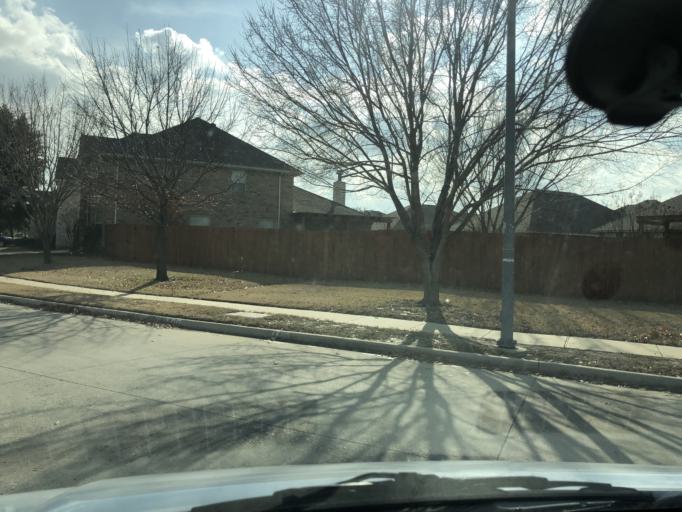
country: US
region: Texas
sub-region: Tarrant County
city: Saginaw
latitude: 32.9182
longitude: -97.3672
